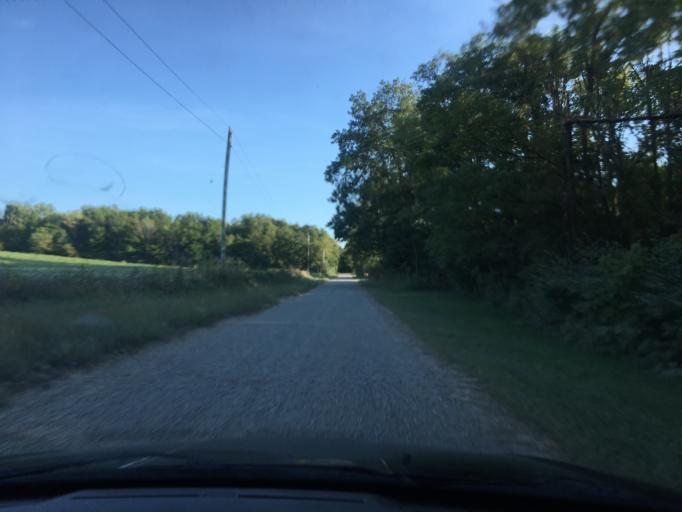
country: US
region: Ohio
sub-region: Logan County
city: West Liberty
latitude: 40.2305
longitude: -83.6633
